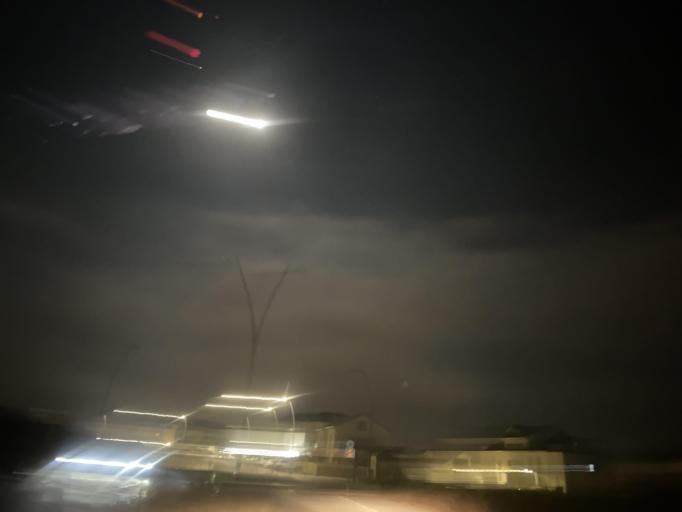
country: IL
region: Haifa
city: Daliyat el Karmil
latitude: 32.6361
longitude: 35.0746
